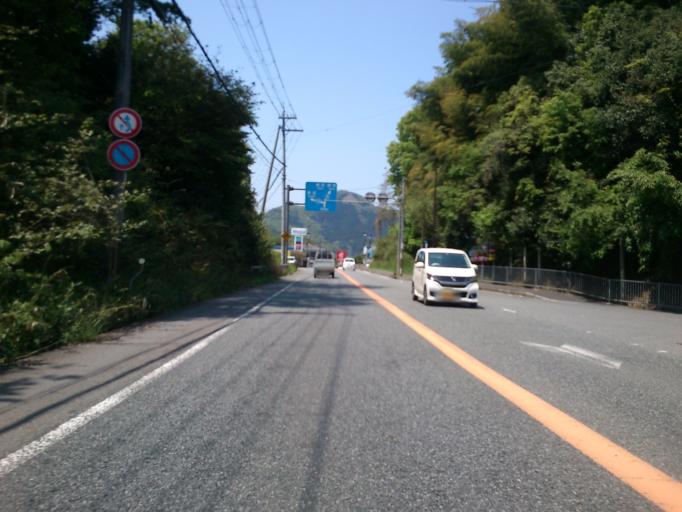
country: JP
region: Kyoto
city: Fukuchiyama
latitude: 35.3032
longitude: 135.1071
